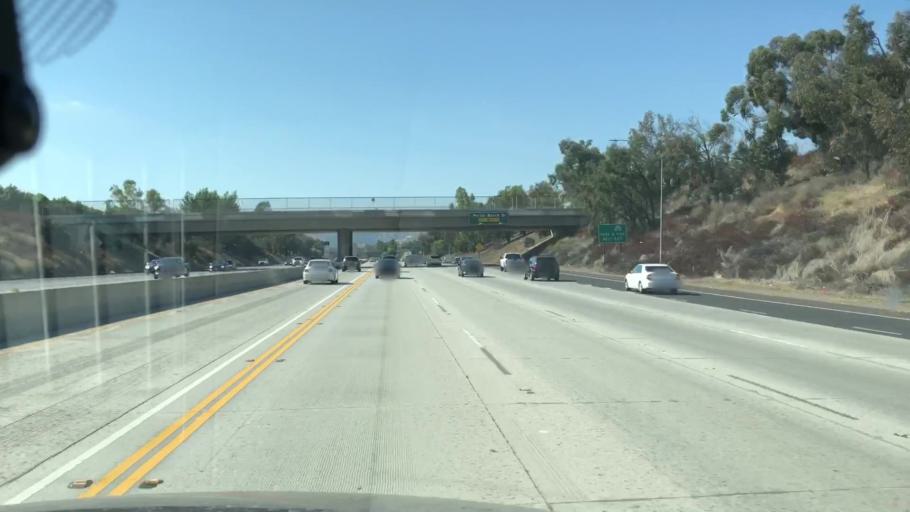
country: US
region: California
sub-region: Los Angeles County
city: Chatsworth
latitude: 34.2731
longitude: -118.5608
